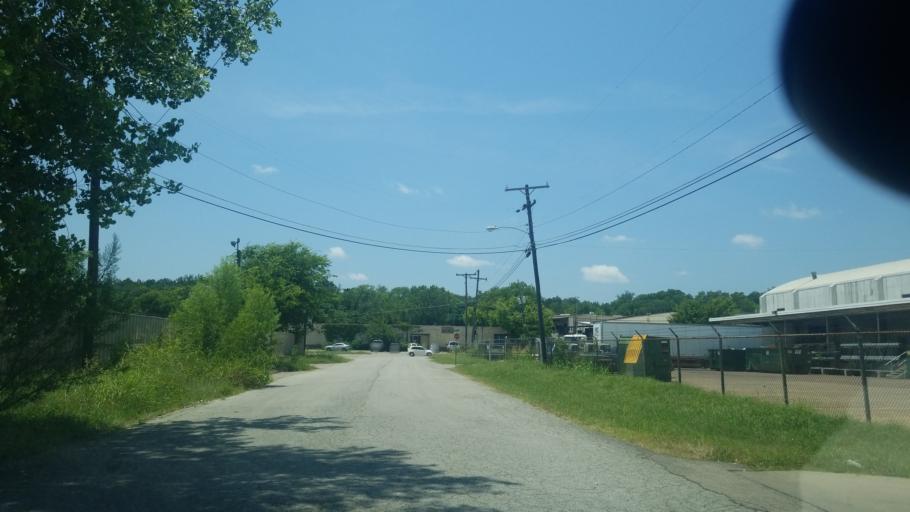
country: US
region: Texas
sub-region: Dallas County
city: Dallas
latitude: 32.7358
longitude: -96.7850
